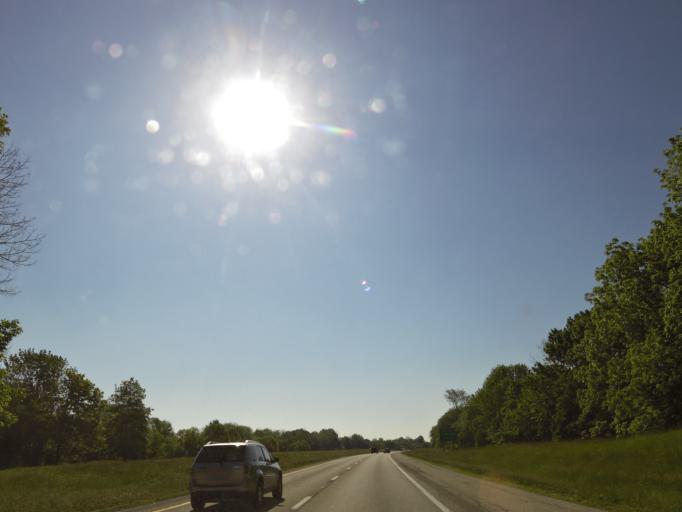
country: US
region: Kentucky
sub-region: Shelby County
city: Shelbyville
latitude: 38.1787
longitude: -85.1740
